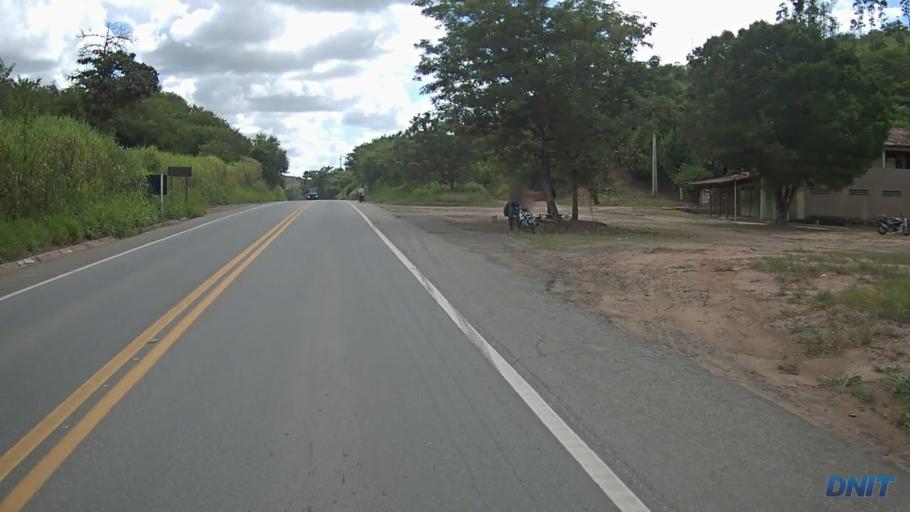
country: BR
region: Minas Gerais
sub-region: Governador Valadares
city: Governador Valadares
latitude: -18.9531
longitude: -42.0729
